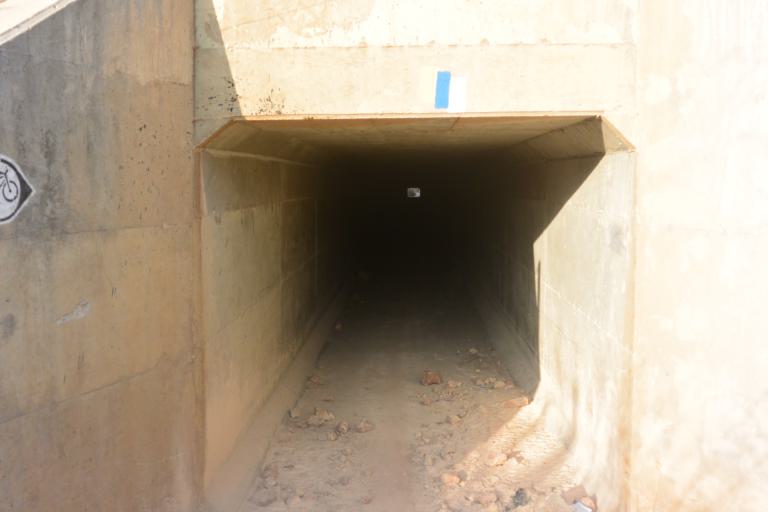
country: PS
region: West Bank
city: Rantis
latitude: 32.0217
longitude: 34.9663
